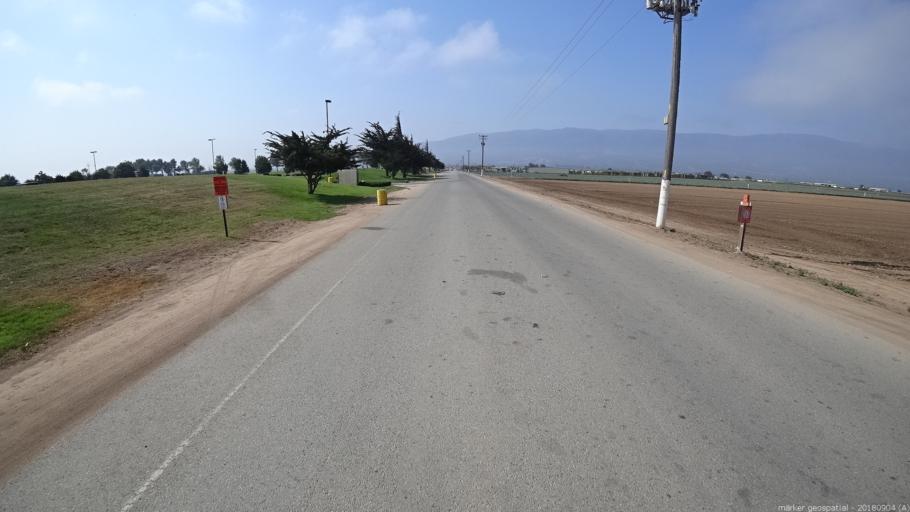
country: US
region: California
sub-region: Monterey County
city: Soledad
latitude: 36.4550
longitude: -121.3566
